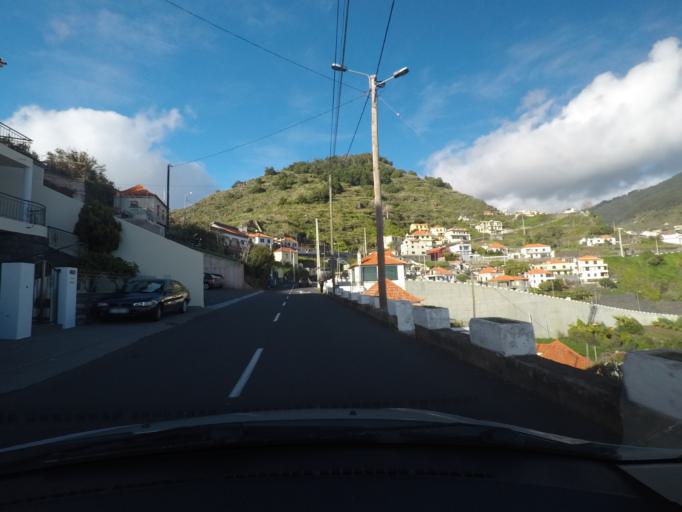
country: PT
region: Madeira
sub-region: Ribeira Brava
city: Campanario
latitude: 32.6673
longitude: -17.0364
